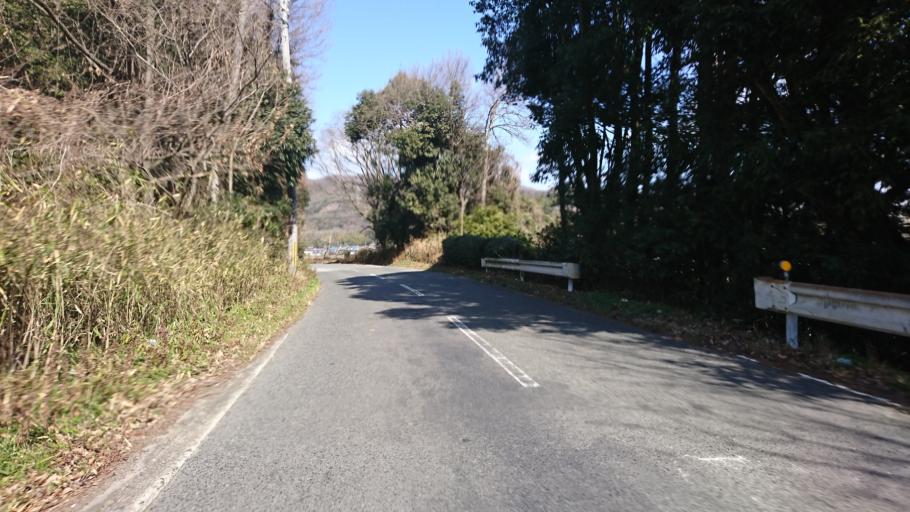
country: JP
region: Hyogo
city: Kakogawacho-honmachi
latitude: 34.8344
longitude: 134.8226
